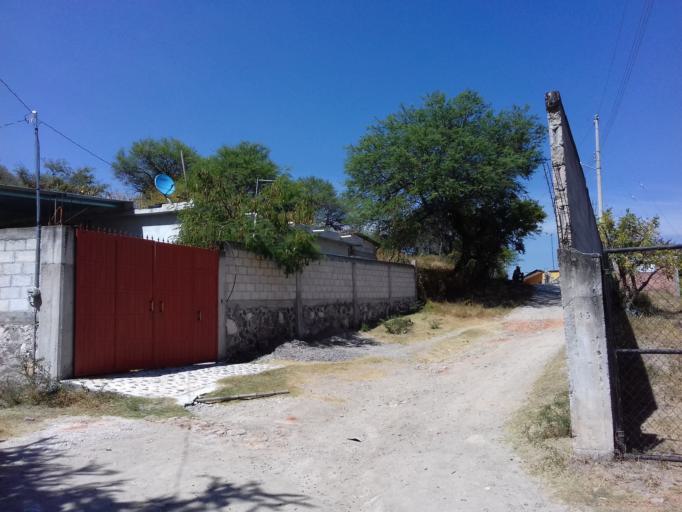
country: MX
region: Morelos
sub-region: Axochiapan
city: Quebrantadero
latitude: 18.5152
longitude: -98.8119
